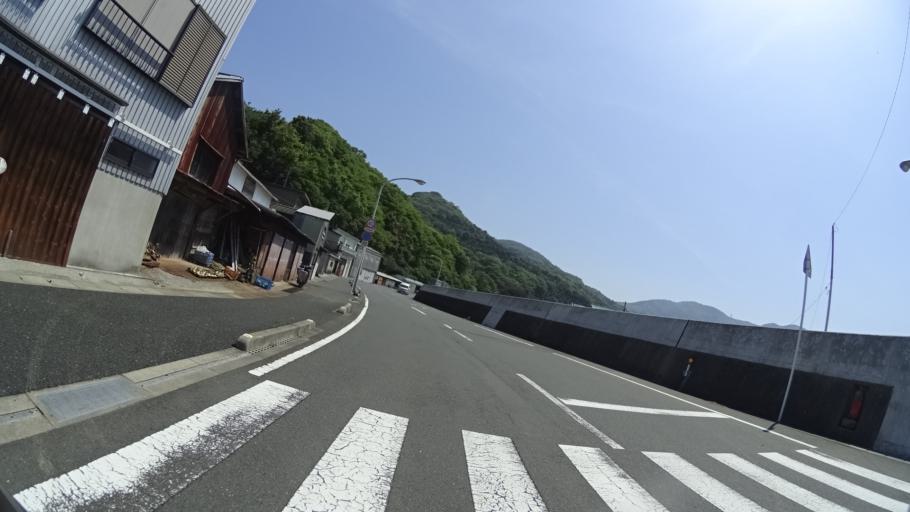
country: JP
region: Ehime
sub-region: Nishiuwa-gun
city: Ikata-cho
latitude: 33.3913
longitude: 132.1146
